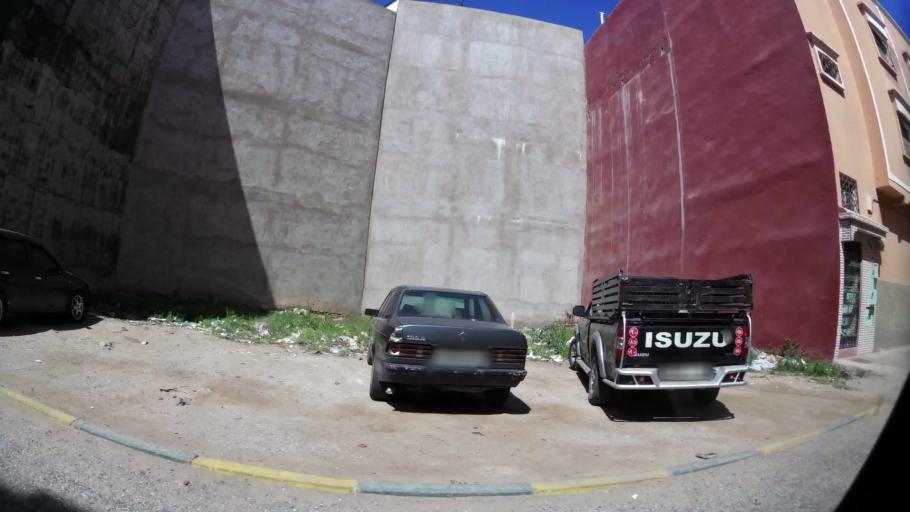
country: MA
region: Souss-Massa-Draa
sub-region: Inezgane-Ait Mellou
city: Inezgane
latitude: 30.3298
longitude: -9.5051
